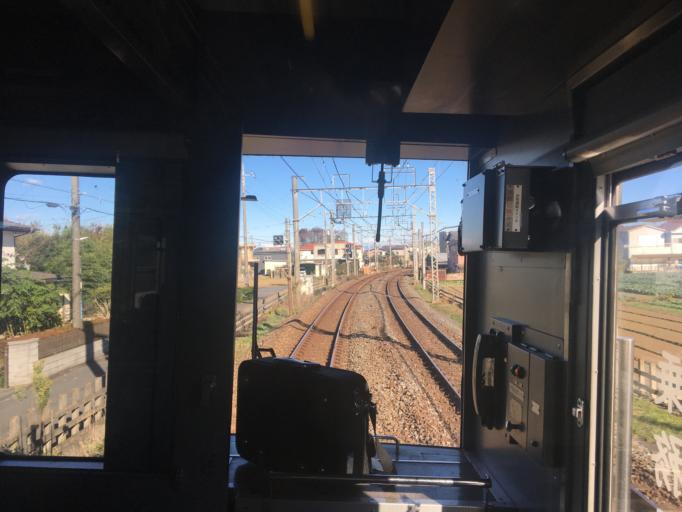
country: JP
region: Saitama
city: Sakado
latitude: 35.9600
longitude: 139.3889
